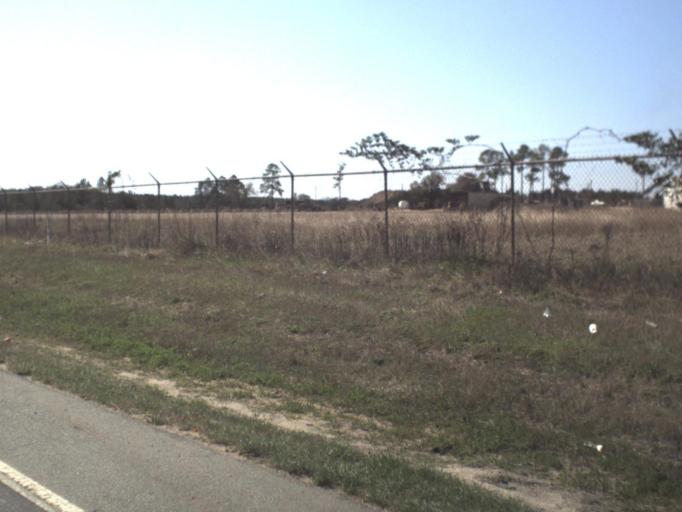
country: US
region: Florida
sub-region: Jackson County
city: Marianna
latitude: 30.6613
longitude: -85.1644
